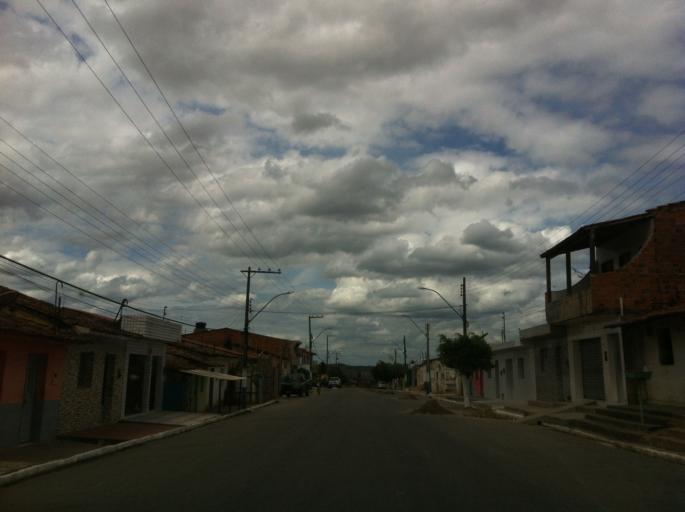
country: BR
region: Alagoas
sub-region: Ibateguara
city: Ibateguara
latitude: -8.9696
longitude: -35.9258
